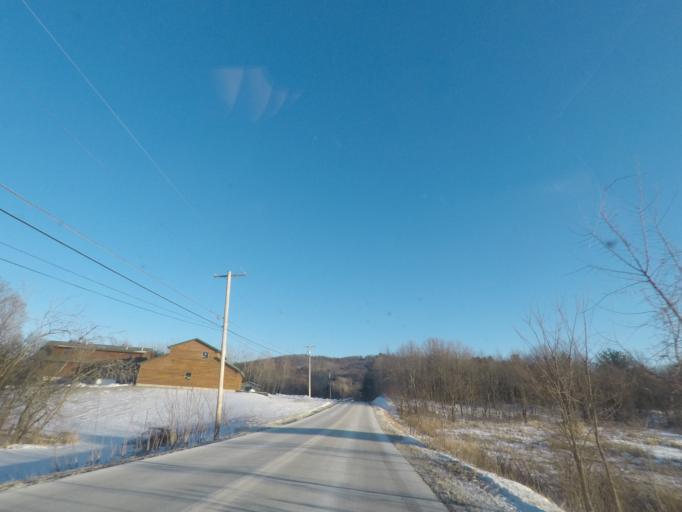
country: US
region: New York
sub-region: Saratoga County
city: Waterford
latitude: 42.8272
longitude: -73.6326
